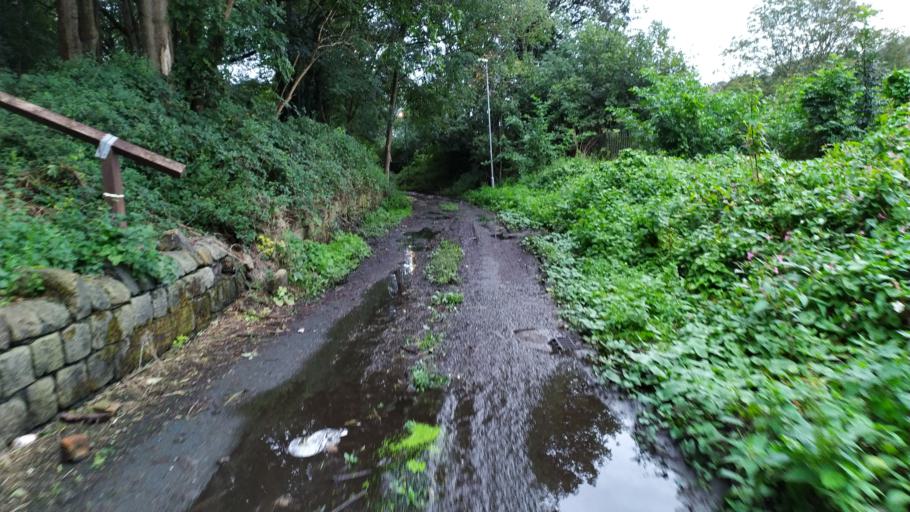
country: GB
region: England
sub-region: City and Borough of Leeds
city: Chapel Allerton
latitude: 53.8158
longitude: -1.5472
